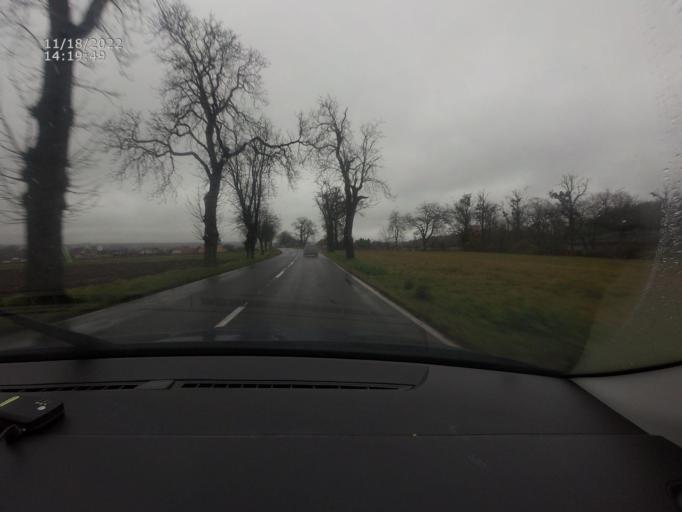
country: CZ
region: Jihocesky
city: Cimelice
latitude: 49.4418
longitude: 14.0787
